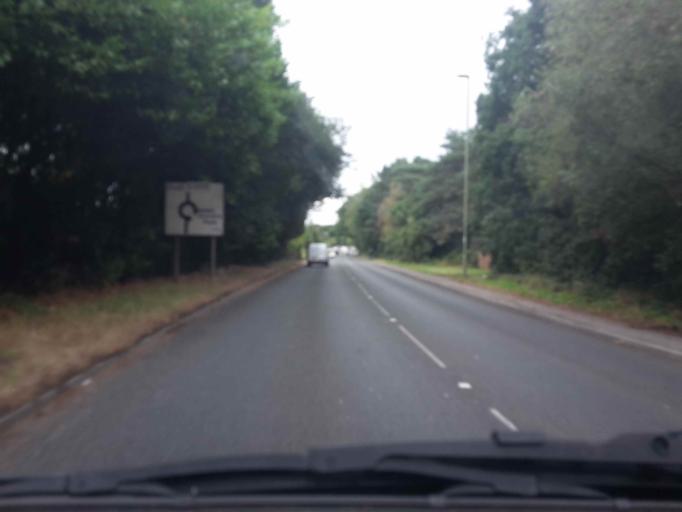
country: GB
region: England
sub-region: Hampshire
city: Fleet
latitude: 51.2918
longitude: -0.8201
